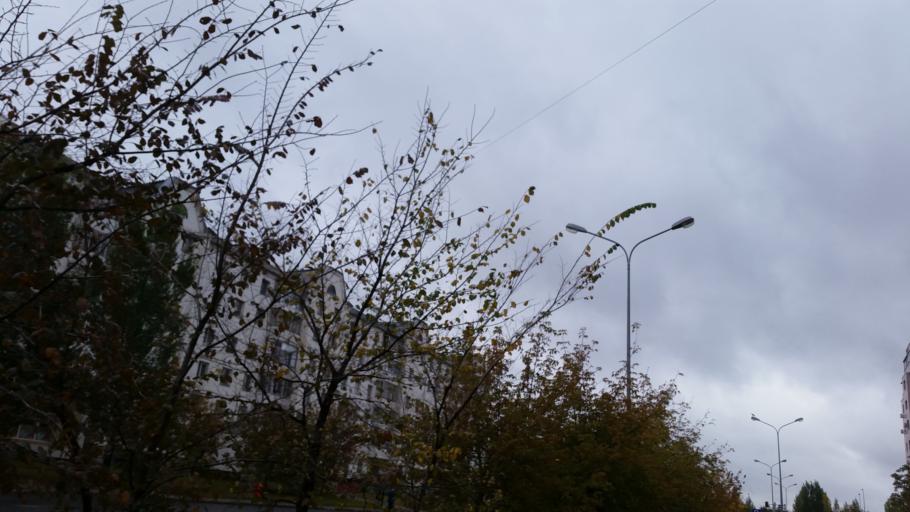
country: KZ
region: Astana Qalasy
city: Astana
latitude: 51.1515
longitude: 71.4997
